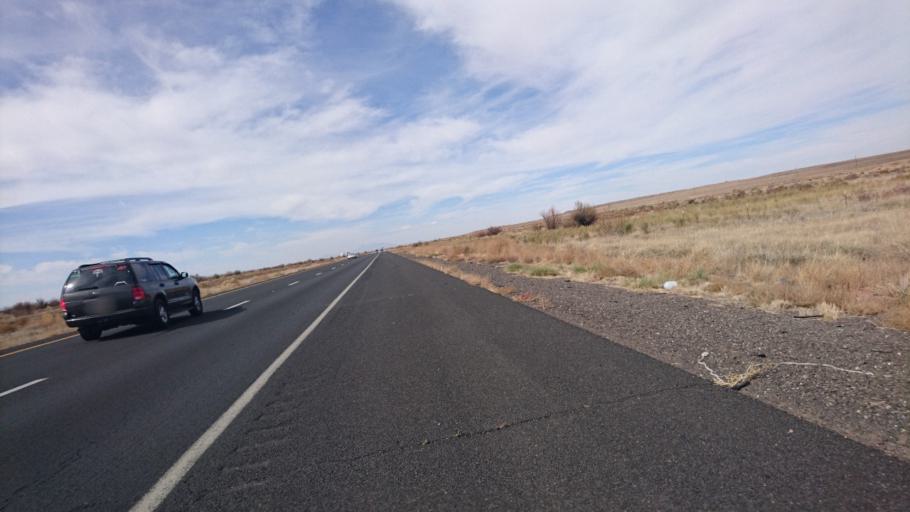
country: US
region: Arizona
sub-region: Navajo County
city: Winslow
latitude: 34.9885
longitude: -110.5639
